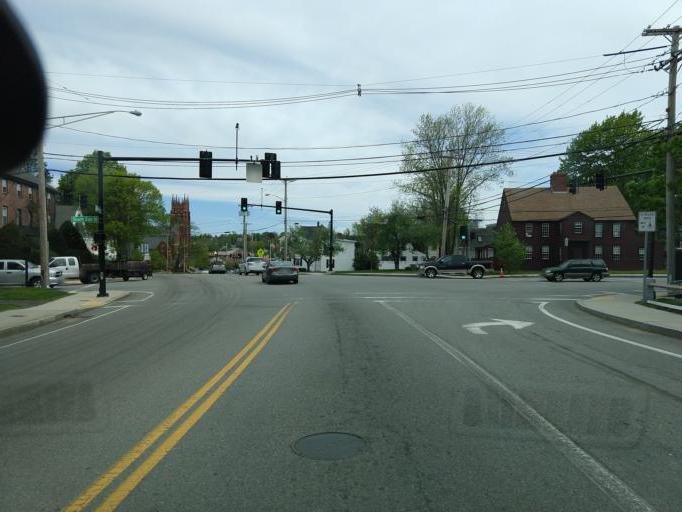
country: US
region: Massachusetts
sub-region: Essex County
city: Haverhill
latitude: 42.7675
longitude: -71.0766
